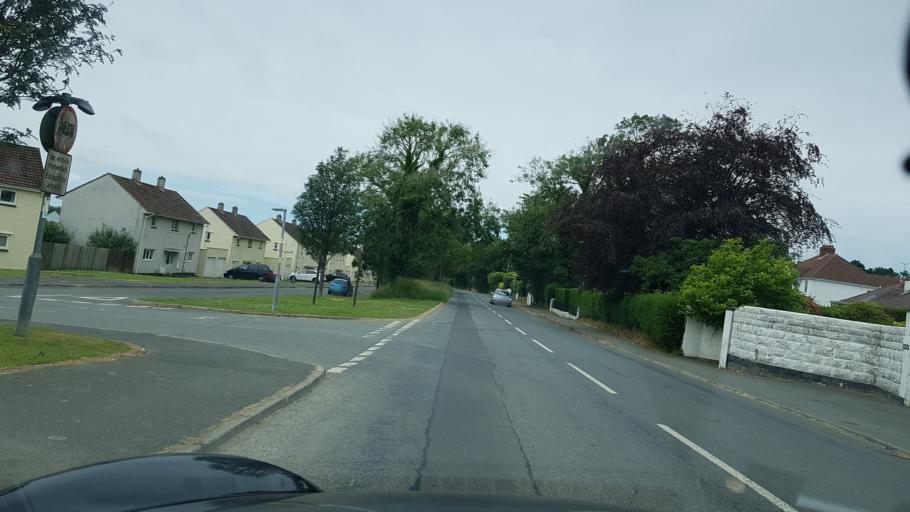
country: GB
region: Wales
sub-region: Pembrokeshire
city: Haverfordwest
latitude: 51.7983
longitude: -4.9874
